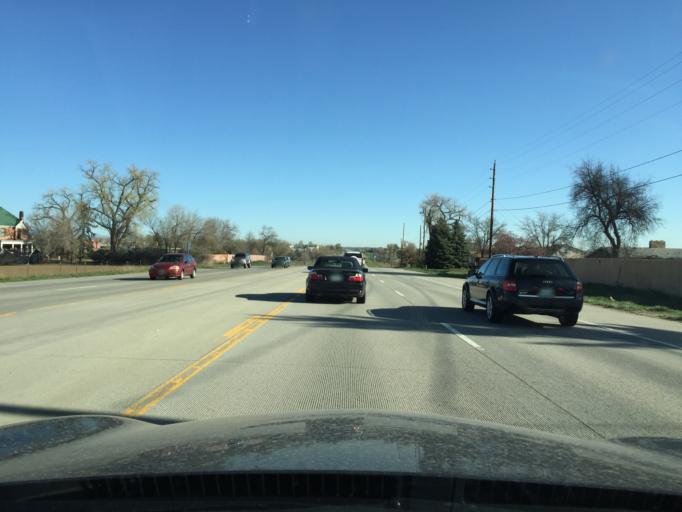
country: US
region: Colorado
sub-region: Boulder County
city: Longmont
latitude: 40.1281
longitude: -105.1026
